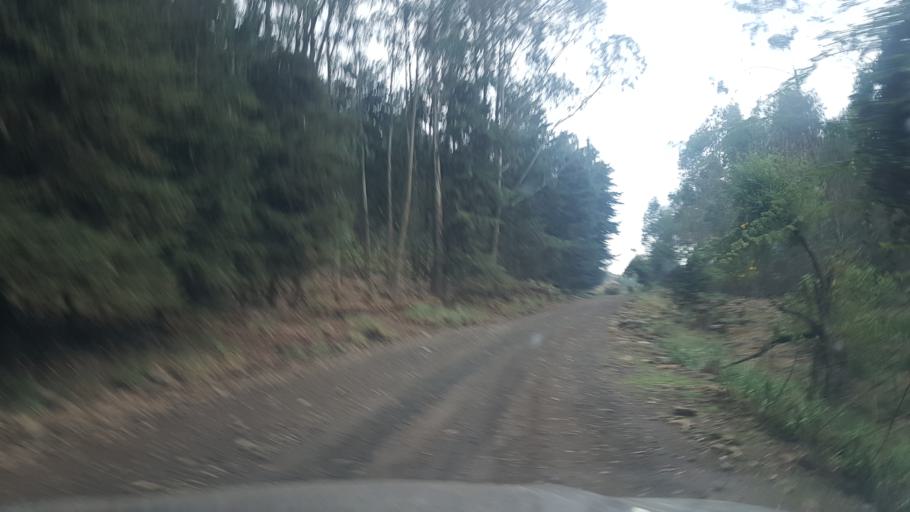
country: ET
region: Amhara
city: Finote Selam
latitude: 10.7867
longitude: 37.6666
